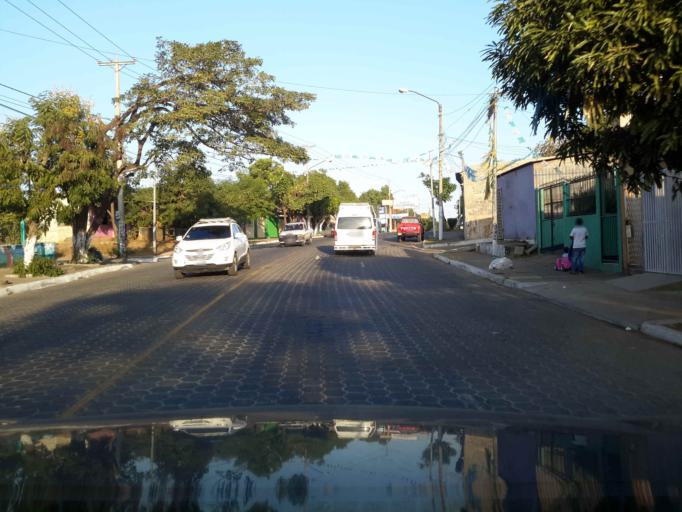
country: NI
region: Managua
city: Ciudad Sandino
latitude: 12.1452
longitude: -86.3016
